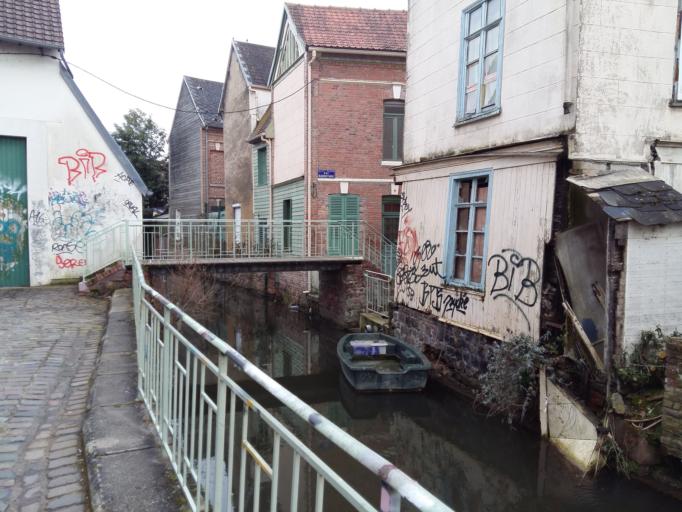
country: FR
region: Picardie
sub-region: Departement de la Somme
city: Amiens
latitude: 49.8989
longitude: 2.3043
